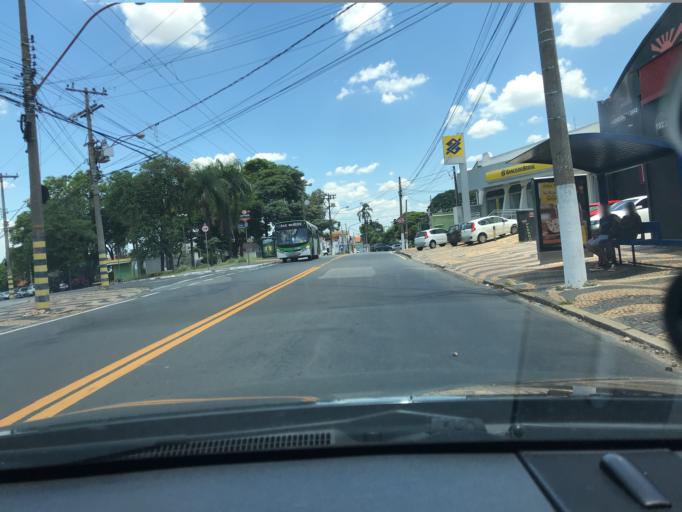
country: BR
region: Sao Paulo
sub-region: Campinas
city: Campinas
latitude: -22.8805
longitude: -47.0731
